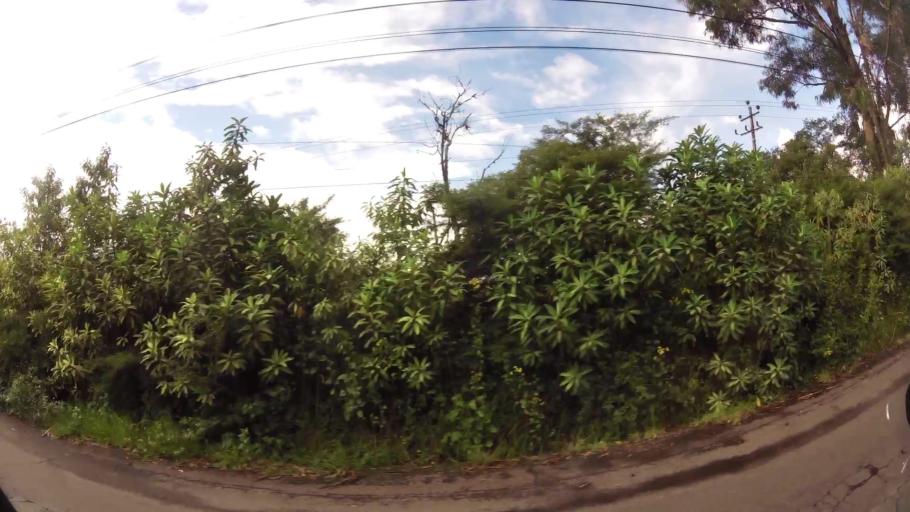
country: EC
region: Pichincha
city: Sangolqui
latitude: -0.3140
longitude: -78.4073
